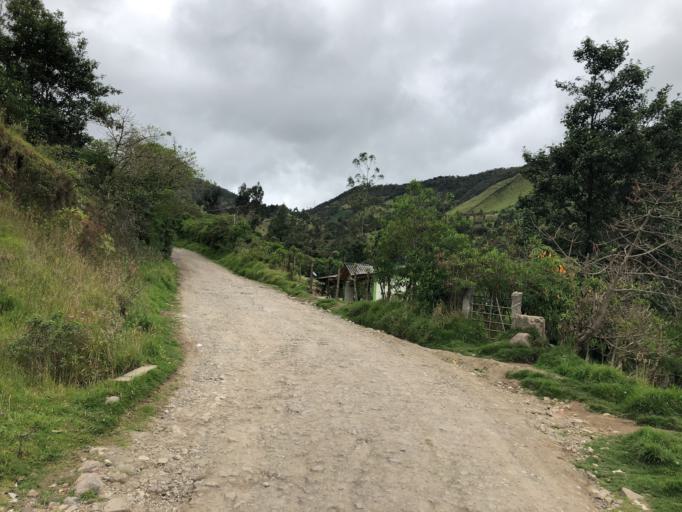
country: CO
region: Cauca
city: Totoro
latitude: 2.5108
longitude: -76.3726
